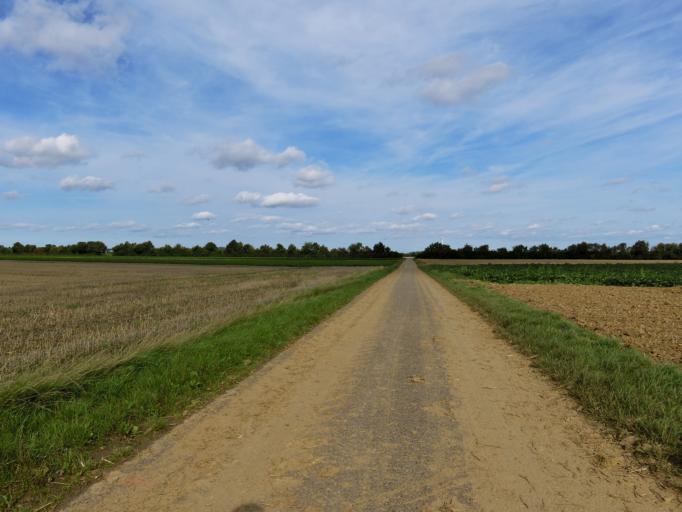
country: DE
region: North Rhine-Westphalia
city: Niedermerz
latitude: 50.8491
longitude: 6.2521
